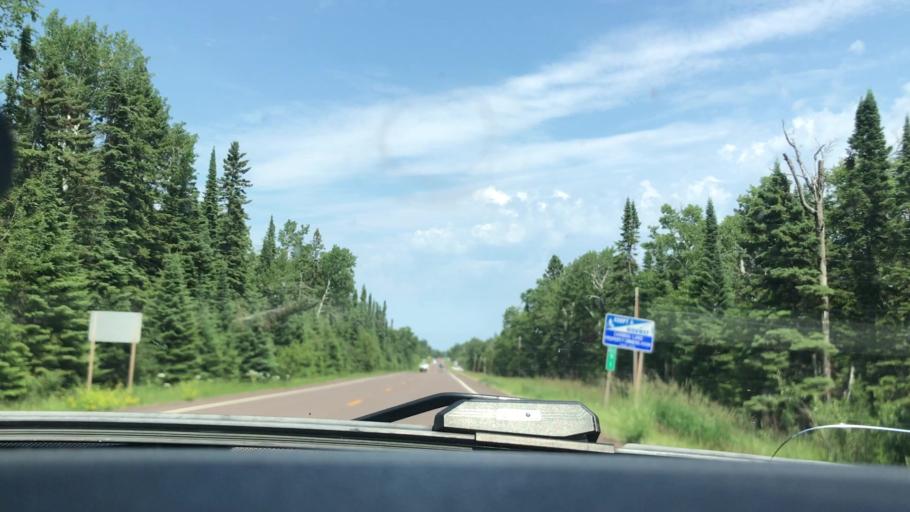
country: US
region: Minnesota
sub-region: Cook County
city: Grand Marais
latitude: 47.6434
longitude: -90.6901
